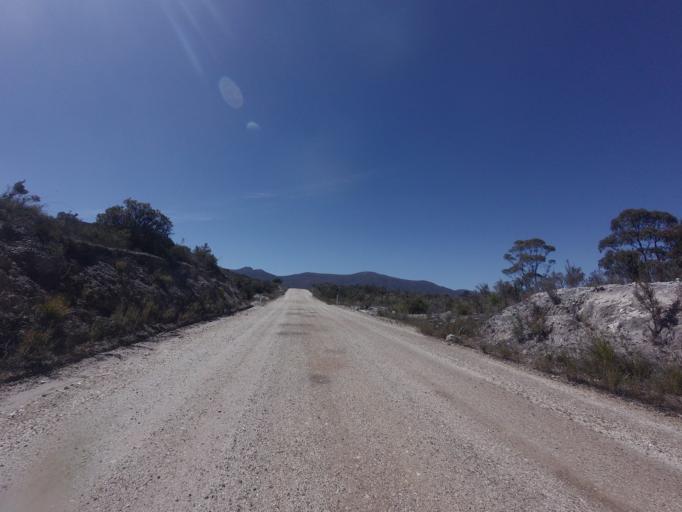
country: AU
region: Tasmania
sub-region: Huon Valley
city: Geeveston
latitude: -43.0353
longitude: 146.3137
